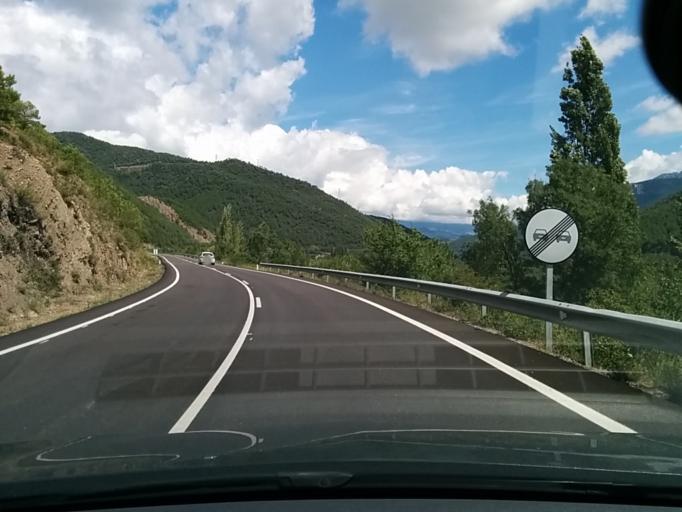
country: ES
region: Aragon
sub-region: Provincia de Huesca
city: Labuerda
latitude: 42.4549
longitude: 0.1364
